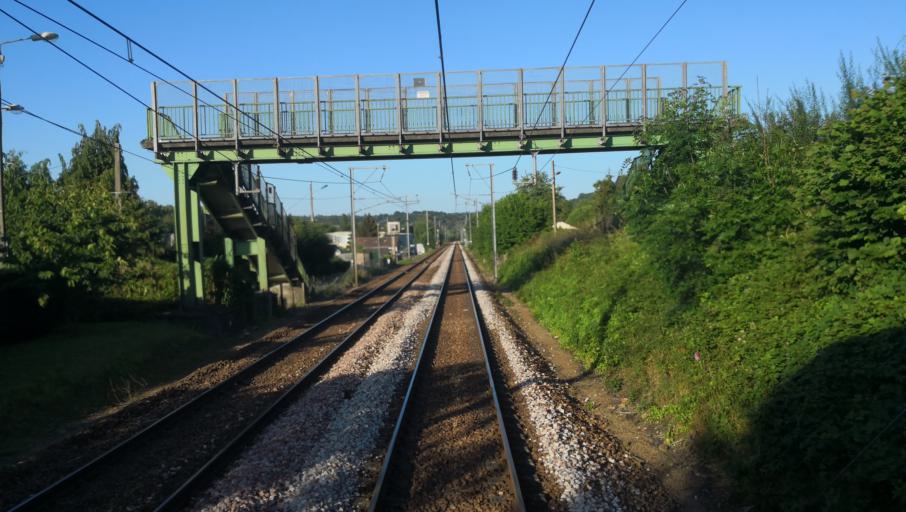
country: FR
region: Haute-Normandie
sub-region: Departement de l'Eure
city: Menneval
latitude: 49.0930
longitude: 0.6158
